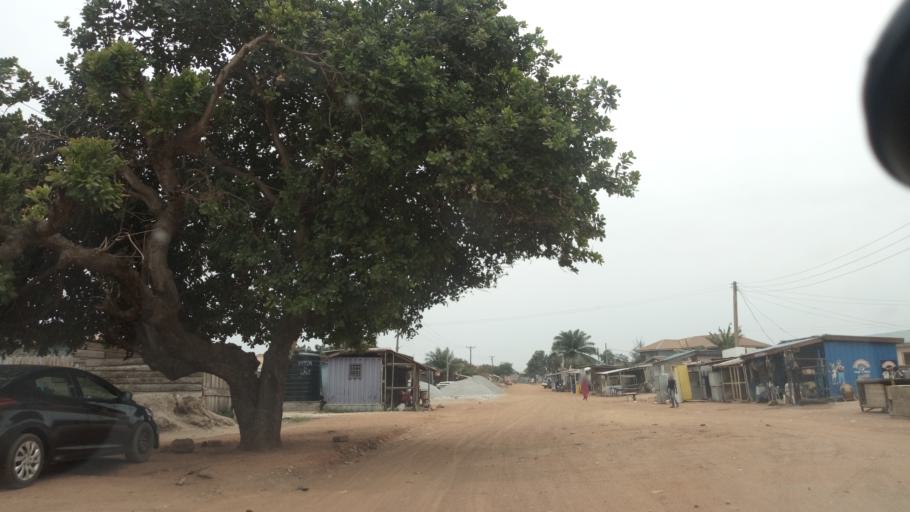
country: GH
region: Greater Accra
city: Medina Estates
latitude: 5.7053
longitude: -0.1335
